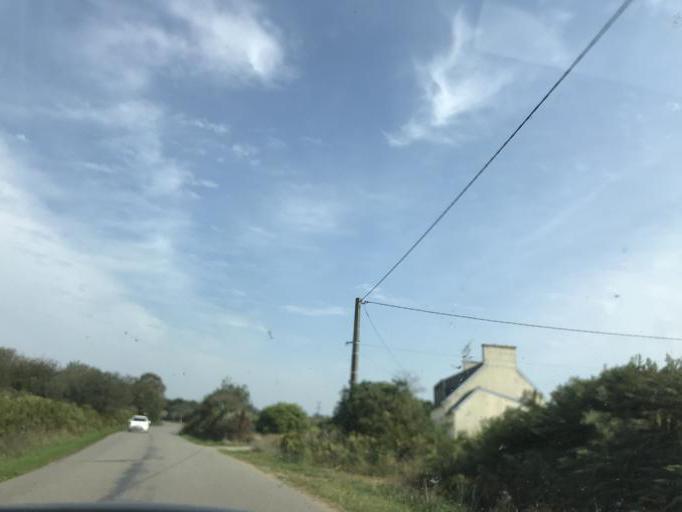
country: FR
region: Brittany
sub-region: Departement du Finistere
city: Hanvec
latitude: 48.2872
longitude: -4.1144
